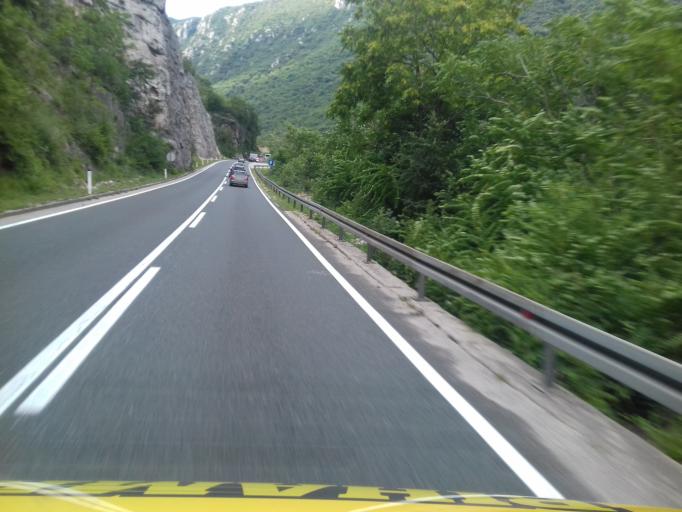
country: BA
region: Federation of Bosnia and Herzegovina
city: Jablanica
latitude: 43.5624
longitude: 17.7202
